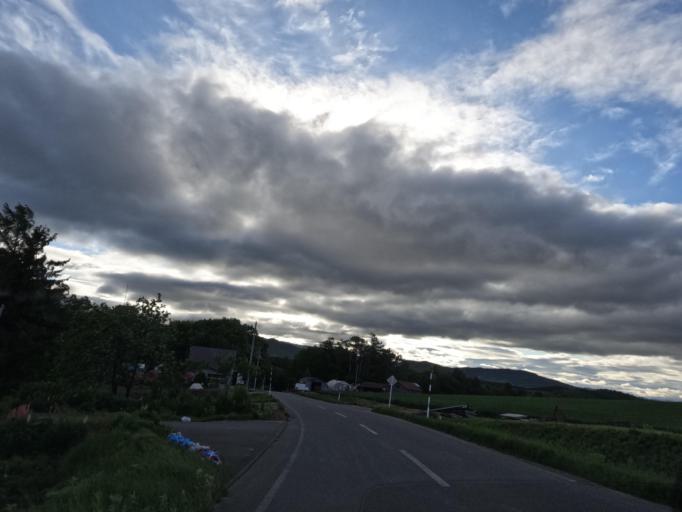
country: JP
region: Hokkaido
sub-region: Asahikawa-shi
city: Asahikawa
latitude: 43.6332
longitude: 142.4234
